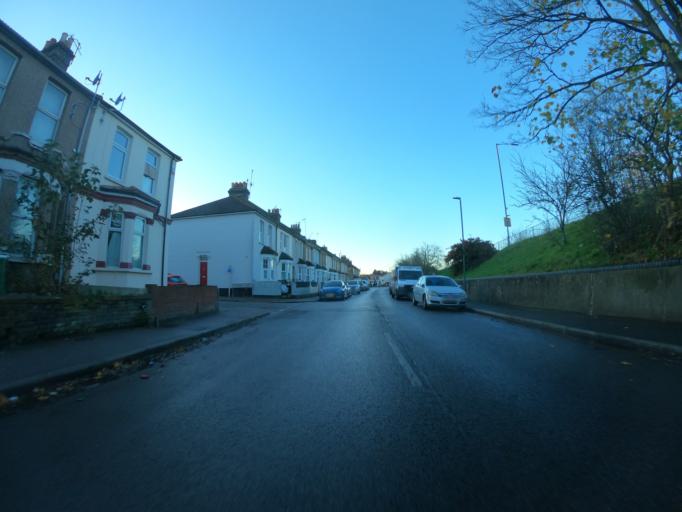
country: GB
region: England
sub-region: Greater London
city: Erith
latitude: 51.4895
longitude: 0.1643
